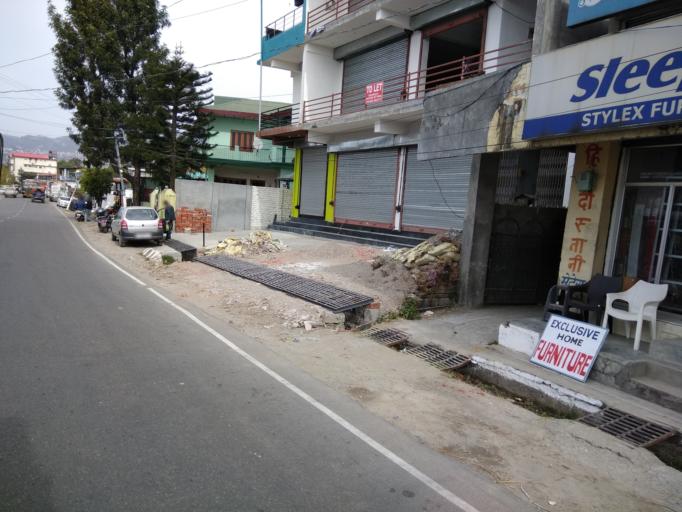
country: IN
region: Himachal Pradesh
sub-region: Kangra
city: Dharmsala
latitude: 32.1915
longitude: 76.3500
